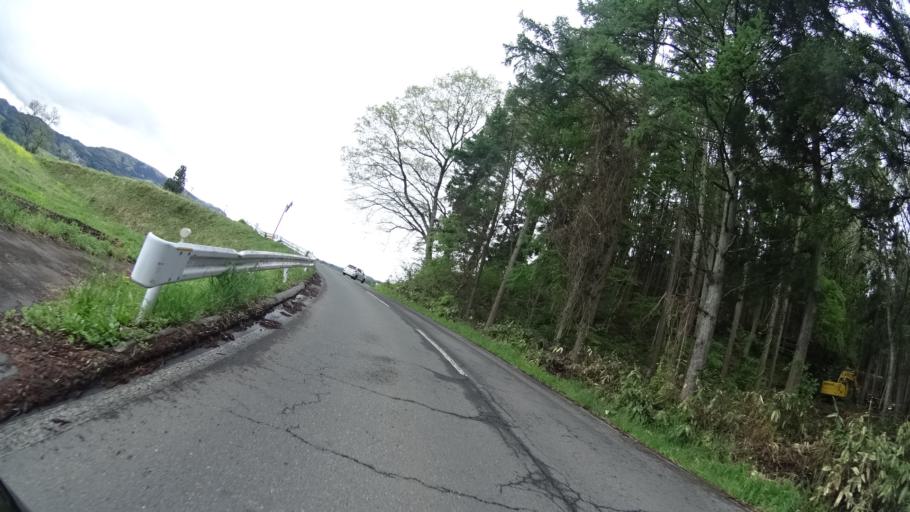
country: JP
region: Nagano
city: Nagano-shi
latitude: 36.7482
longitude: 138.2045
